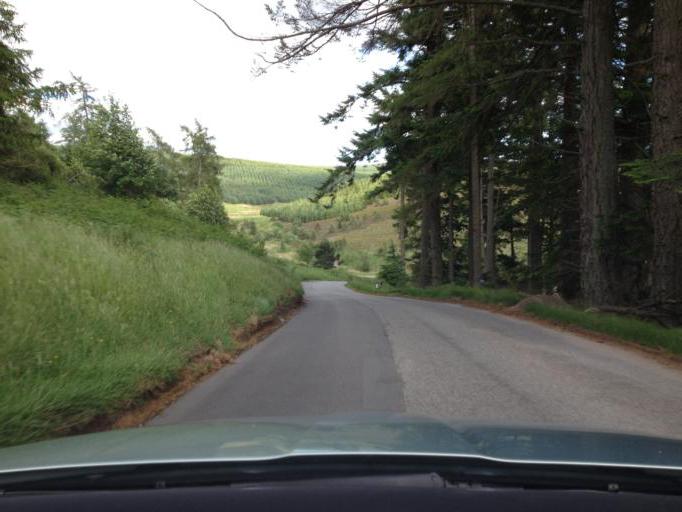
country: GB
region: Scotland
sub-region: Aberdeenshire
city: Banchory
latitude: 56.9513
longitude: -2.5841
